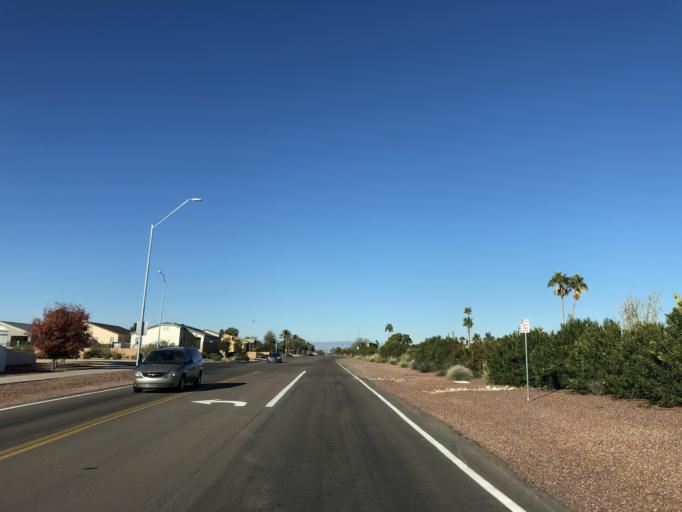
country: US
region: Arizona
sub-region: Maricopa County
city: Sun City West
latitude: 33.6592
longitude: -112.2900
